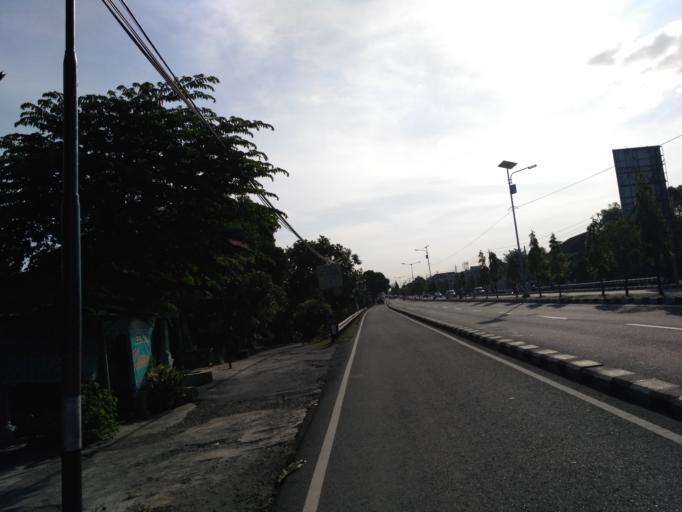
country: ID
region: Daerah Istimewa Yogyakarta
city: Depok
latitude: -7.7658
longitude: 110.4293
